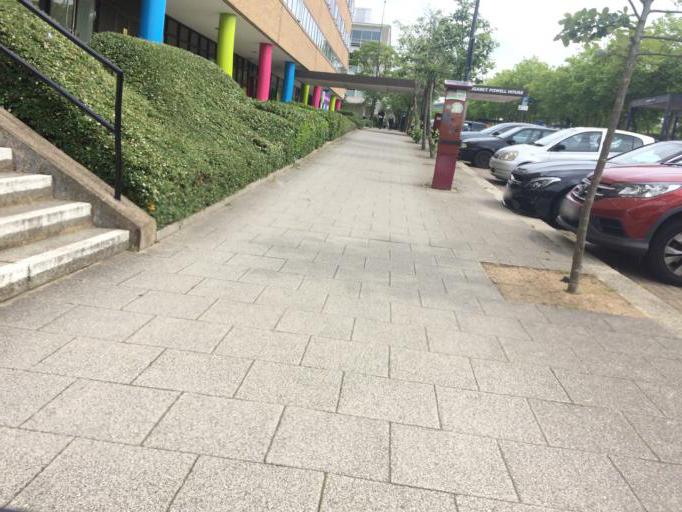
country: GB
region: England
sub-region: Milton Keynes
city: Milton Keynes
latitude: 52.0398
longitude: -0.7624
